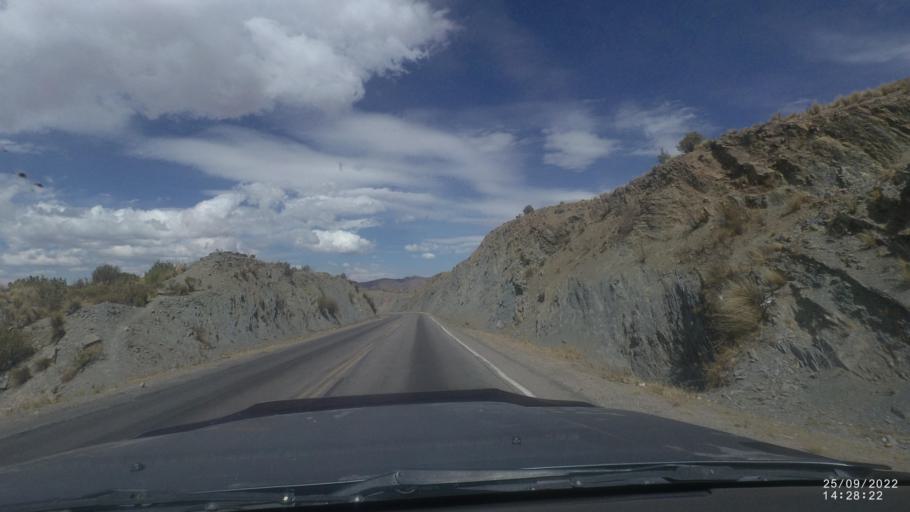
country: BO
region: Cochabamba
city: Sipe Sipe
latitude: -17.7111
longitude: -66.6700
